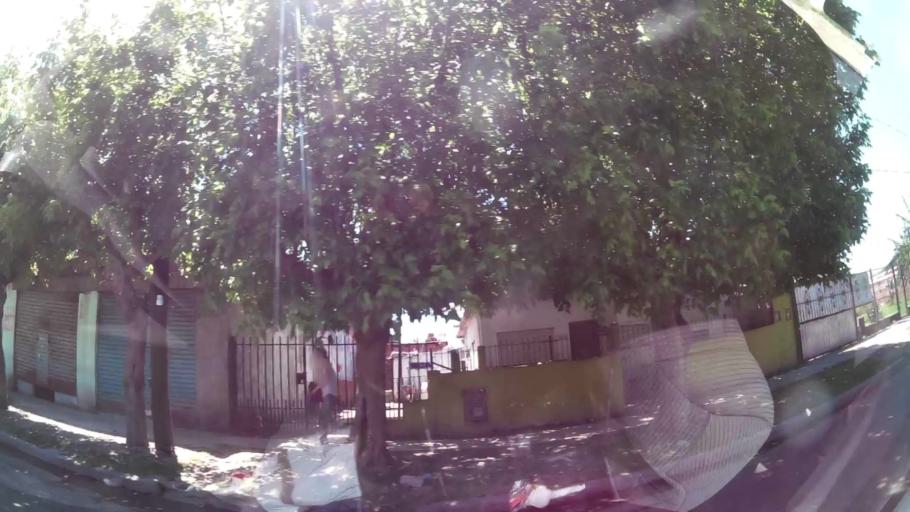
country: AR
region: Buenos Aires
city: Hurlingham
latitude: -34.4888
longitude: -58.6636
